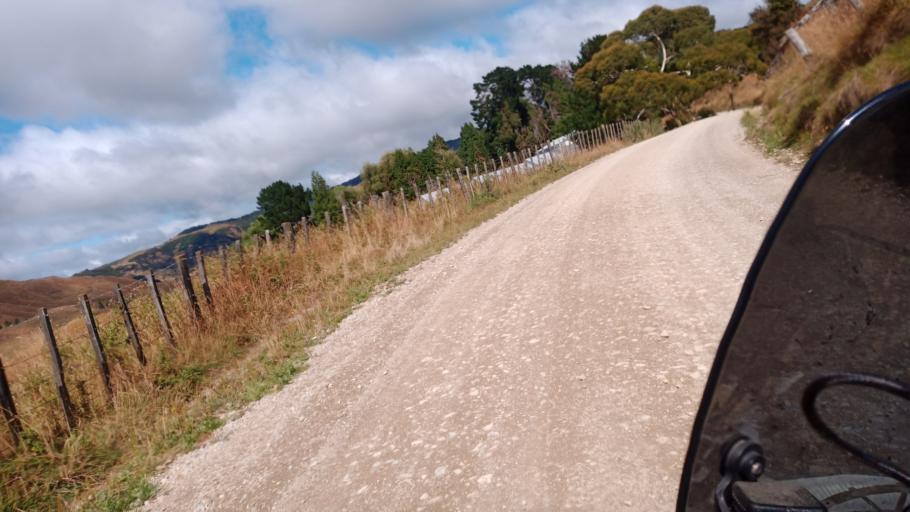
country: NZ
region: Hawke's Bay
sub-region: Wairoa District
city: Wairoa
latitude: -38.6075
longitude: 177.4511
